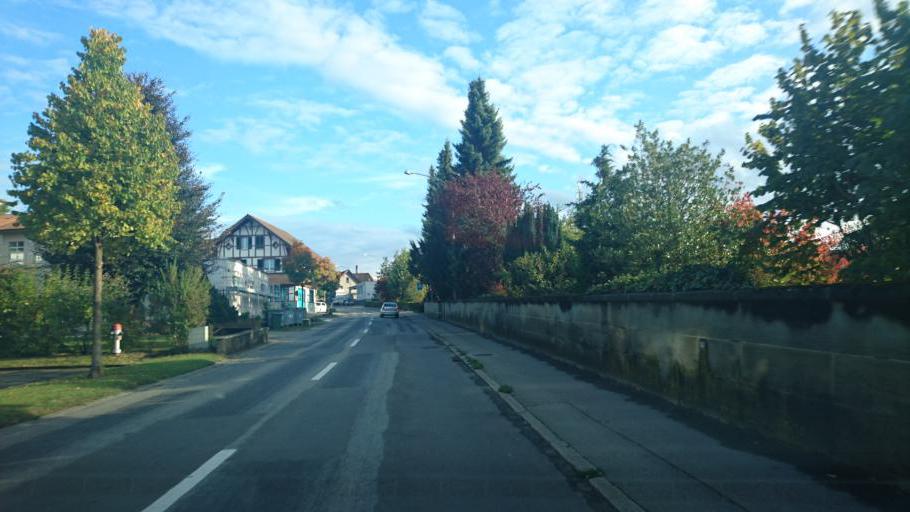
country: CH
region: Bern
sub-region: Bern-Mittelland District
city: Worb
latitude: 46.9321
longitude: 7.5606
